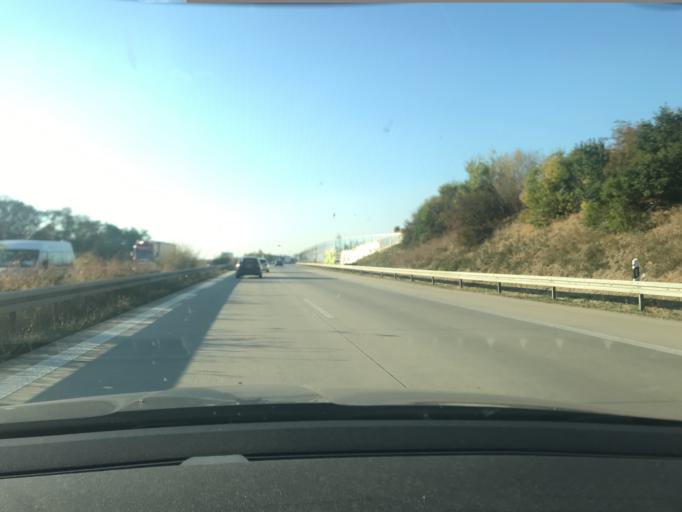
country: DE
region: Saxony
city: Kreischa
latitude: 50.9868
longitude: 13.7784
